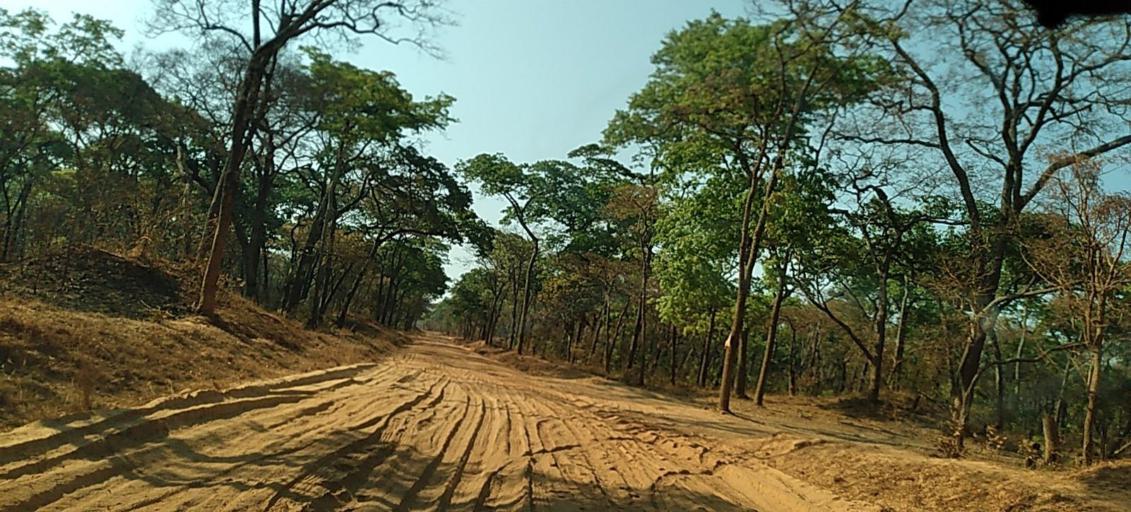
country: ZM
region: North-Western
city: Kasempa
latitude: -13.6307
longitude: 25.9883
